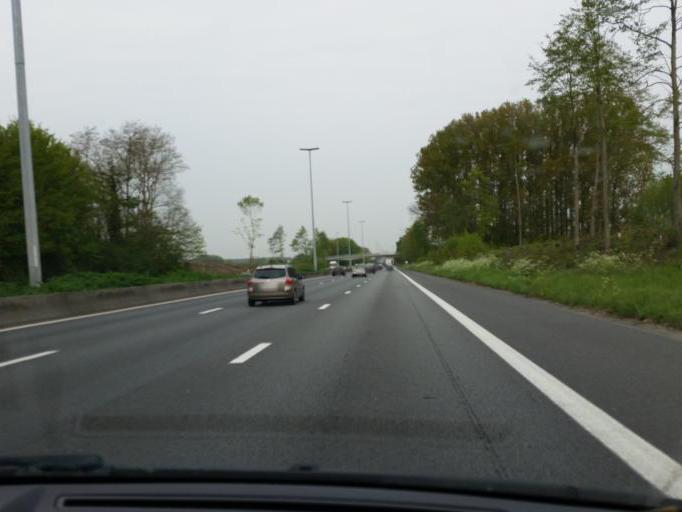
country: BE
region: Flanders
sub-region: Provincie Oost-Vlaanderen
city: Sint-Lievens-Houtem
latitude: 50.9526
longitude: 3.8856
